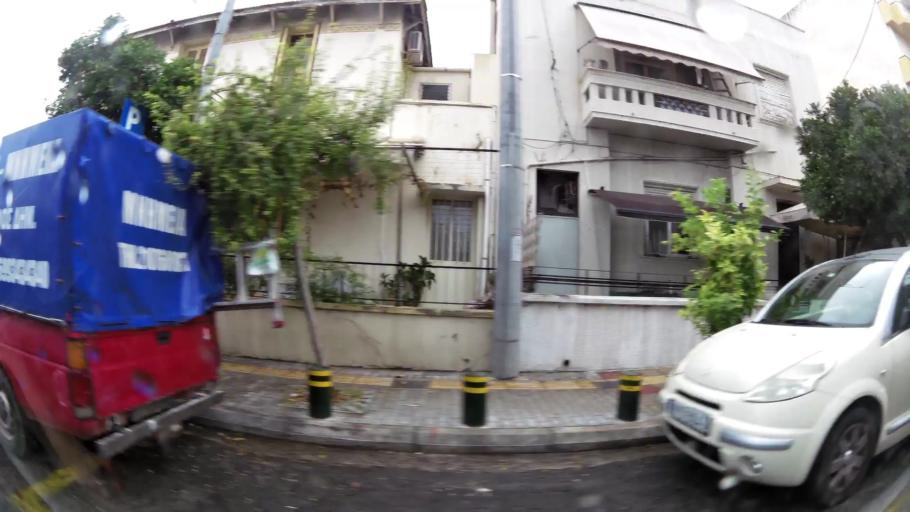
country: GR
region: Attica
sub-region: Nomarchia Athinas
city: Ymittos
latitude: 37.9549
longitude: 23.7467
